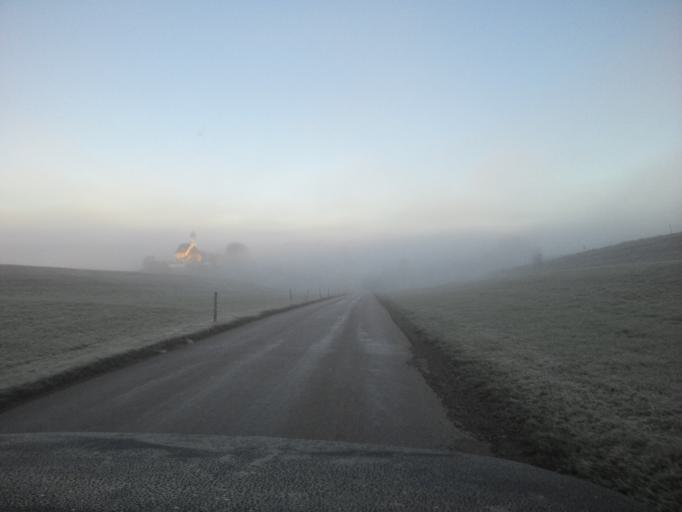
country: DE
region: Bavaria
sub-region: Upper Bavaria
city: Seeshaupt
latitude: 47.8330
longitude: 11.2441
